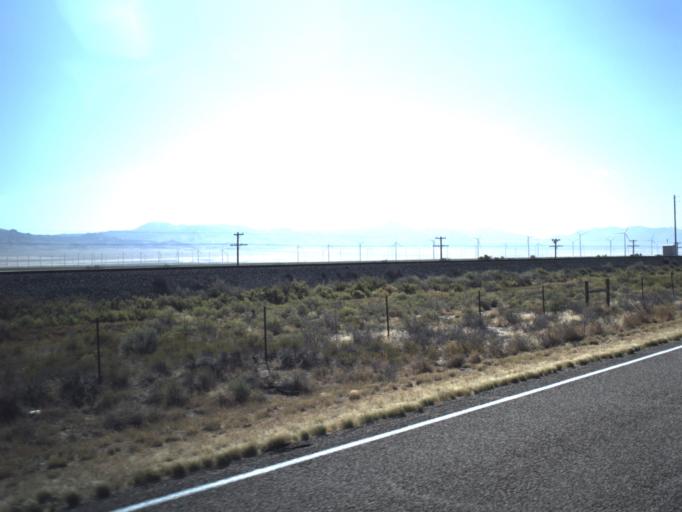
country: US
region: Utah
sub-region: Beaver County
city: Milford
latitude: 38.6207
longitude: -112.9852
